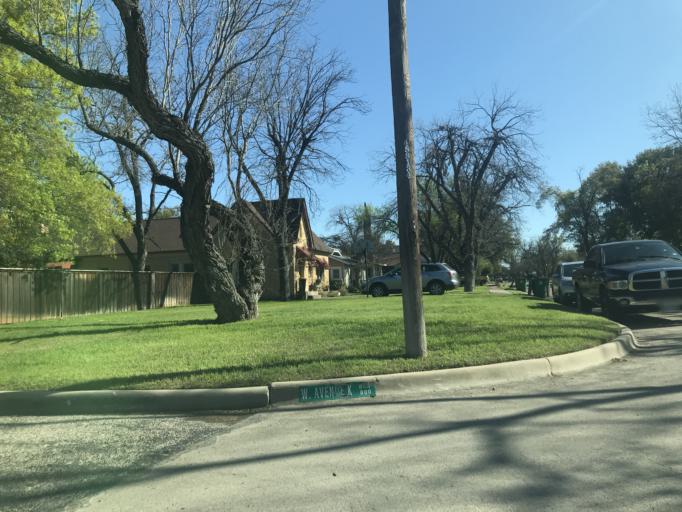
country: US
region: Texas
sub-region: Tom Green County
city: San Angelo
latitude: 31.4462
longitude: -100.4496
